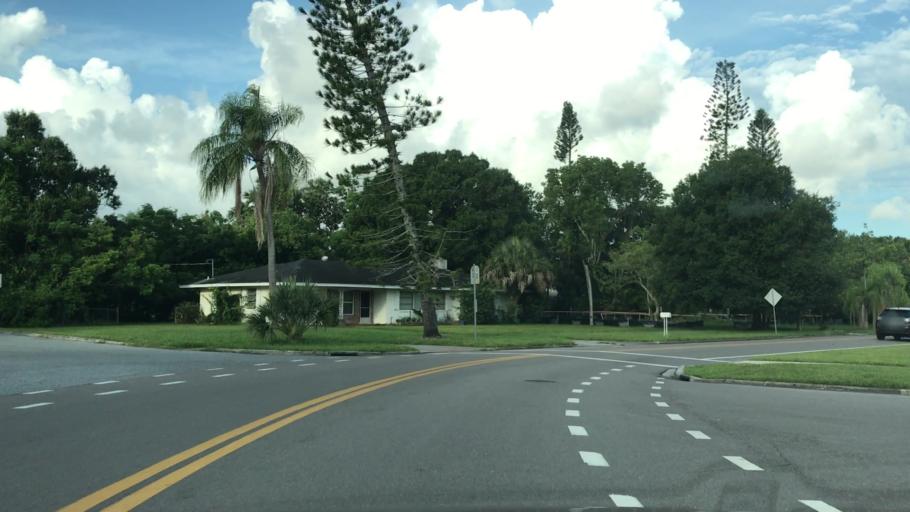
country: US
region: Florida
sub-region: Sarasota County
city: Sarasota
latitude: 27.3357
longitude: -82.5200
